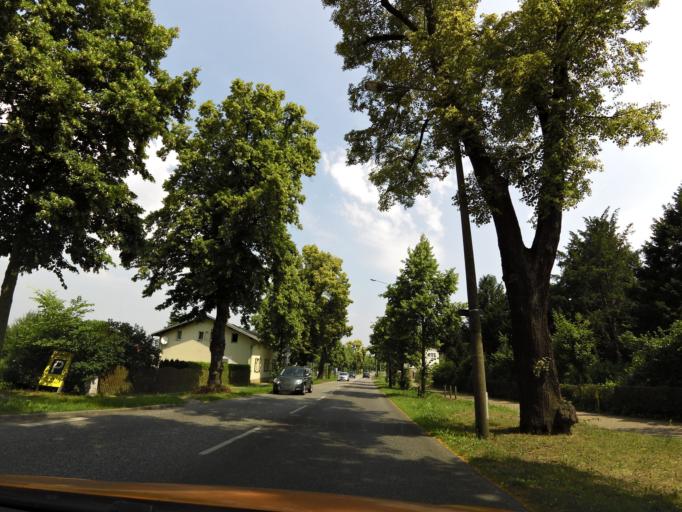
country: DE
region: Brandenburg
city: Potsdam
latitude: 52.4241
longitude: 12.9995
